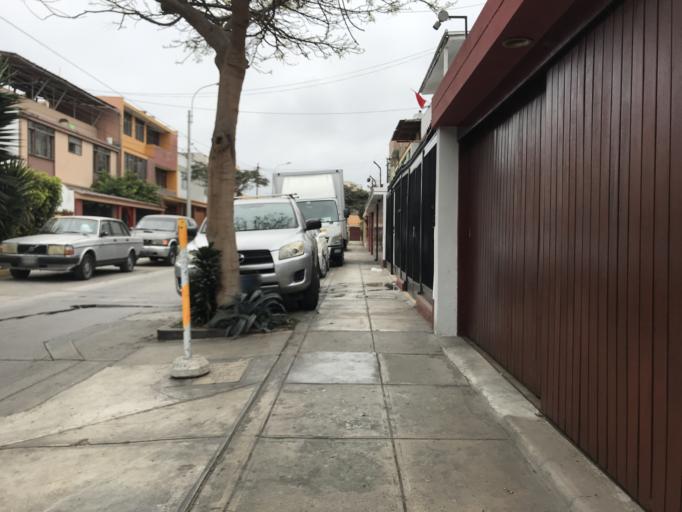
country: PE
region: Lima
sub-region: Lima
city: San Isidro
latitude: -12.0794
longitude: -77.0723
